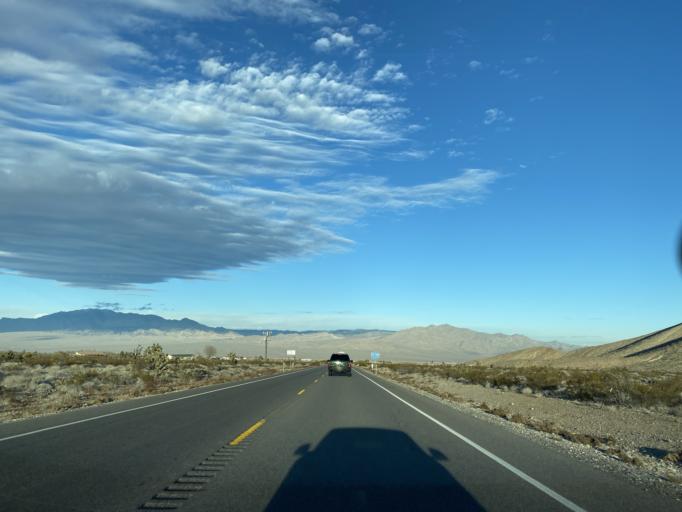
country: US
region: Nevada
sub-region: Clark County
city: Summerlin South
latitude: 36.3011
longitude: -115.4120
